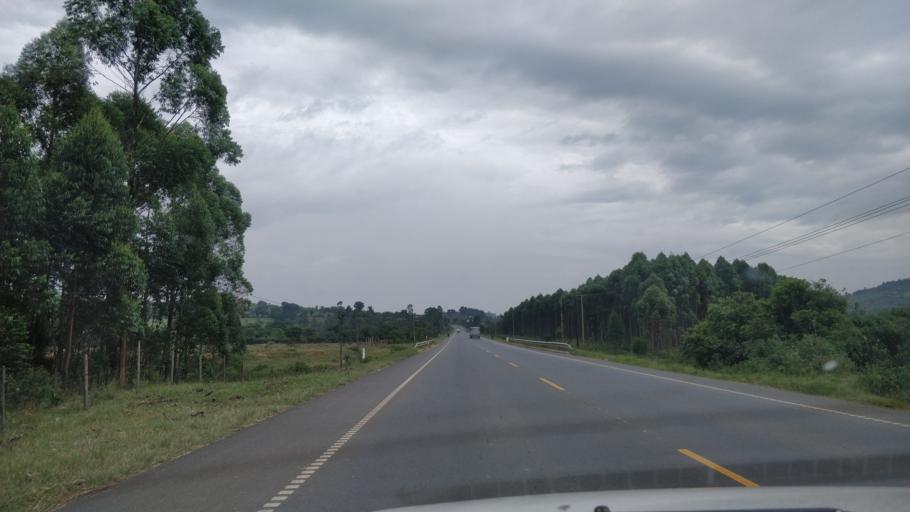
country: UG
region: Western Region
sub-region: Sheema District
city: Kibingo
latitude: -0.6572
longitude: 30.4728
